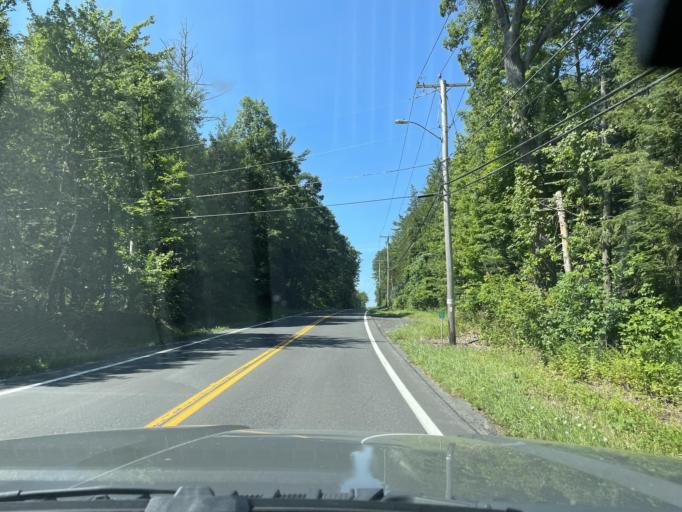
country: US
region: New York
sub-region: Ulster County
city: Manorville
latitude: 42.0811
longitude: -74.0178
